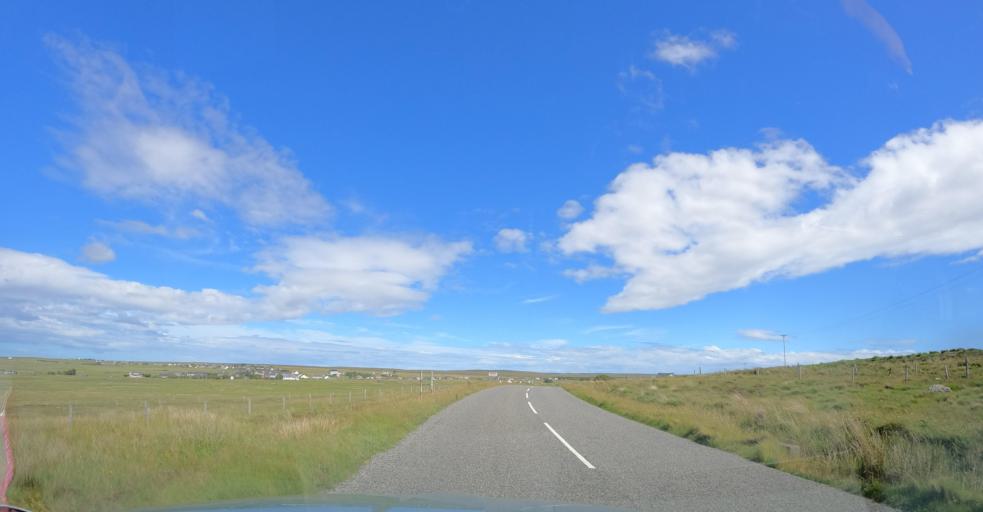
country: GB
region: Scotland
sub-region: Eilean Siar
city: Isle of Lewis
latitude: 58.3494
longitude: -6.5308
